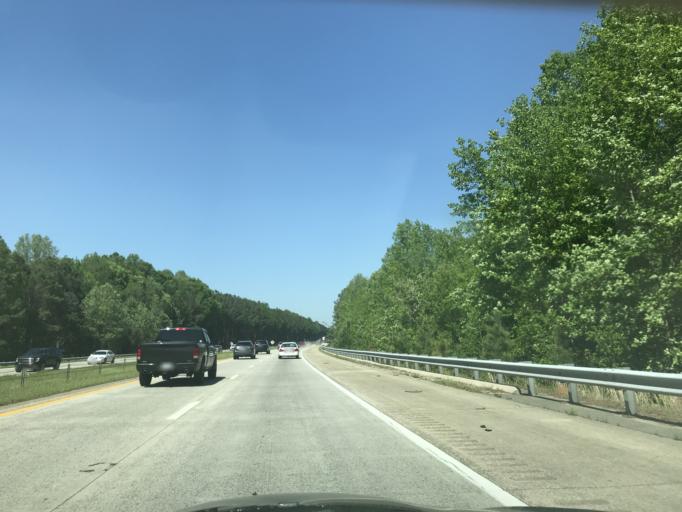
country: US
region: North Carolina
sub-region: Wake County
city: Garner
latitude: 35.5852
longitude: -78.5747
